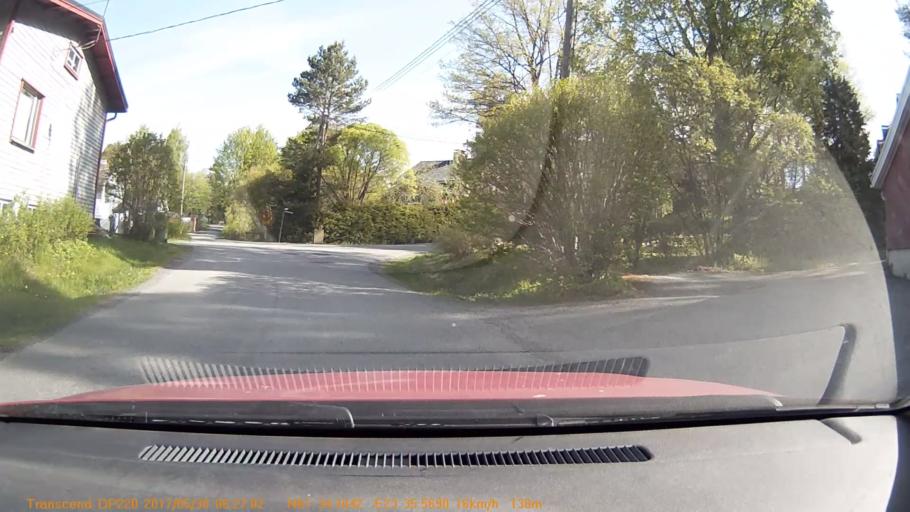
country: FI
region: Pirkanmaa
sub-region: Tampere
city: Yloejaervi
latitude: 61.5694
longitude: 23.5928
